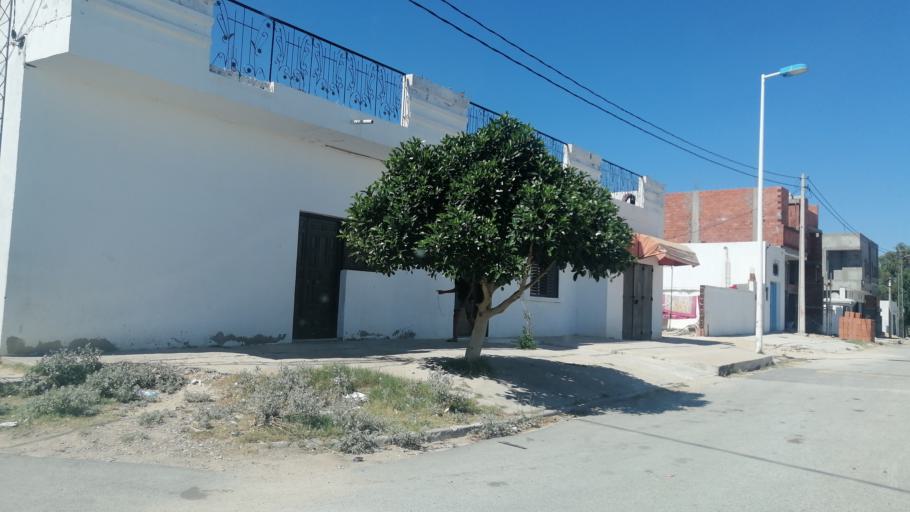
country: TN
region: Al Qayrawan
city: Sbikha
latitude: 36.1248
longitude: 10.0948
